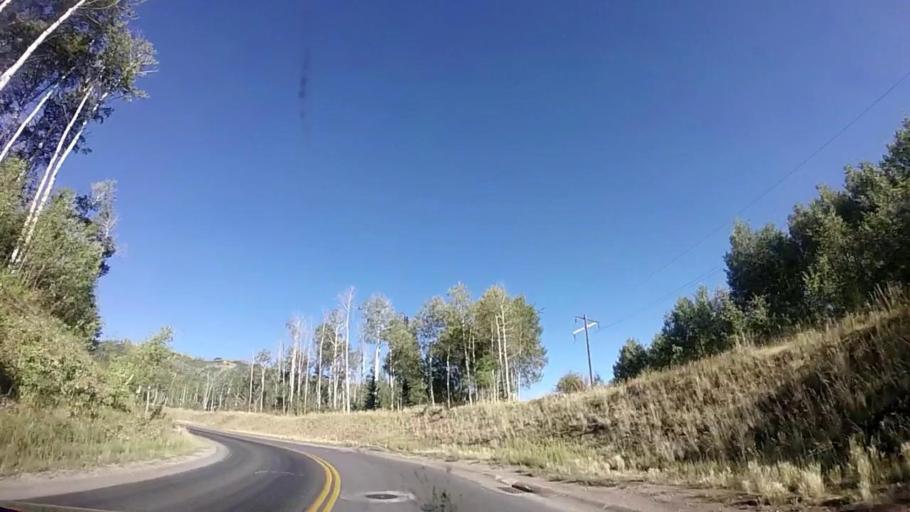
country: US
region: Utah
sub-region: Summit County
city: Park City
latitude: 40.6252
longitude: -111.4998
